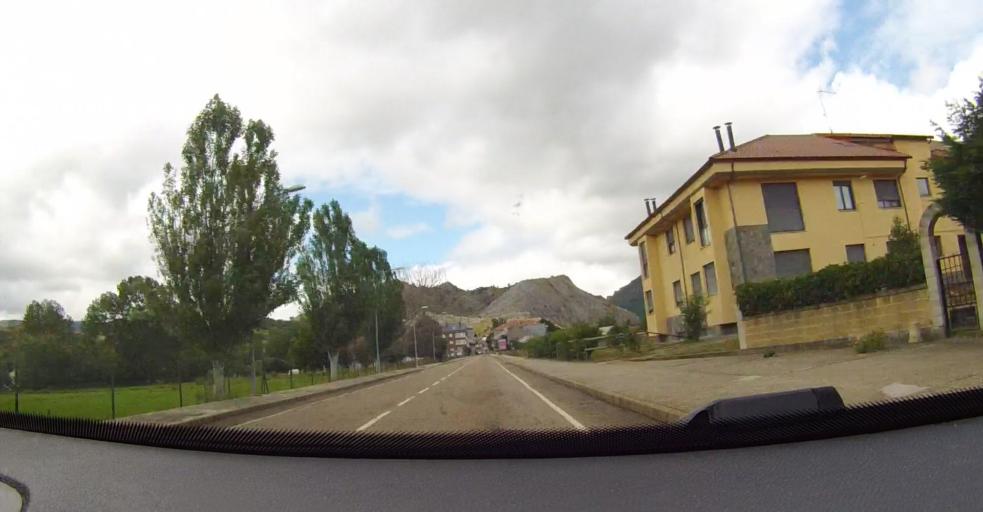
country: ES
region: Castille and Leon
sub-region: Provincia de Leon
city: Puebla de Lillo
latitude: 43.0048
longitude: -5.2699
